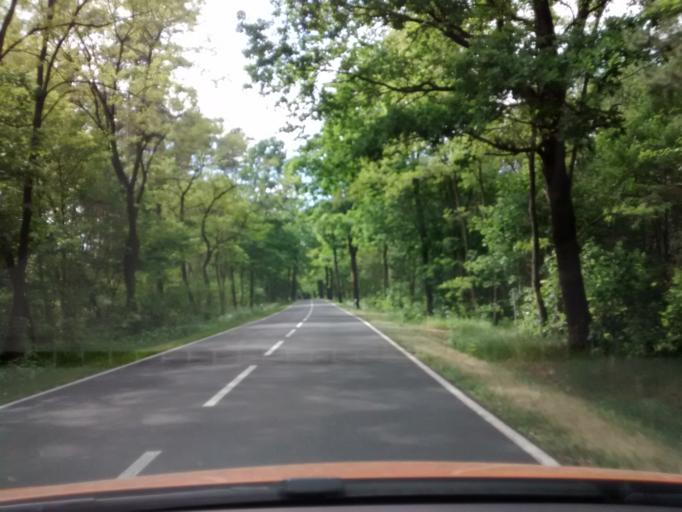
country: DE
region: Brandenburg
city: Ihlow
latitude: 51.9873
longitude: 13.2874
